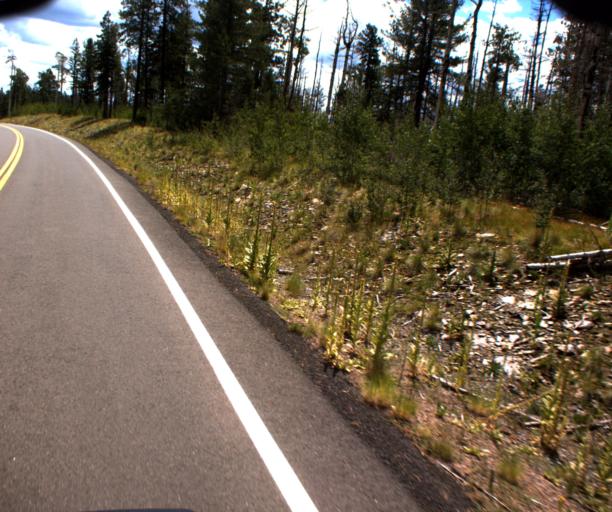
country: US
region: Arizona
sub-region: Apache County
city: Eagar
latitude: 33.9282
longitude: -109.4638
